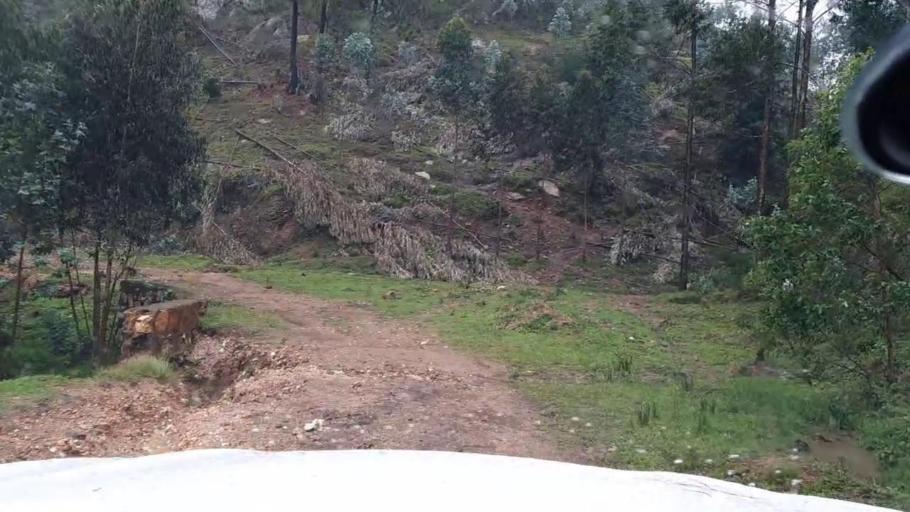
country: RW
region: Western Province
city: Kibuye
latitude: -2.1357
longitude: 29.4573
